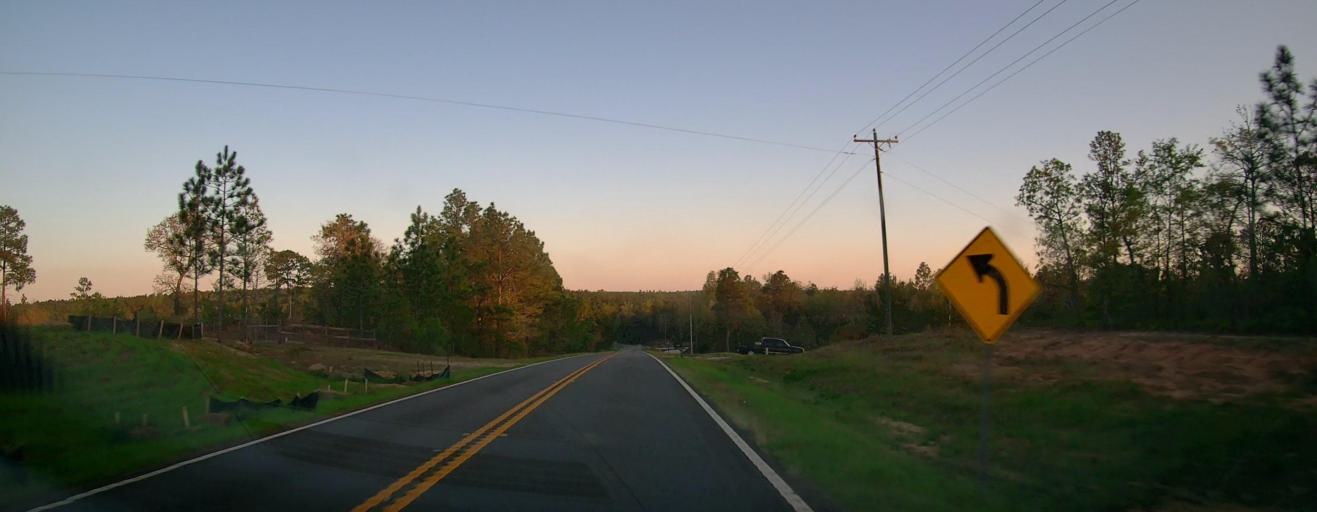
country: US
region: Georgia
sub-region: Marion County
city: Buena Vista
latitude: 32.4497
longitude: -84.6248
